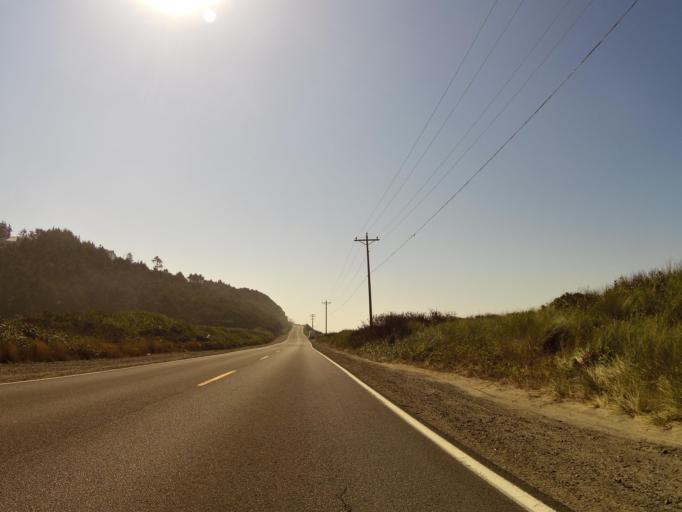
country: US
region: Oregon
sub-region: Tillamook County
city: Pacific City
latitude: 45.2436
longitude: -123.9682
